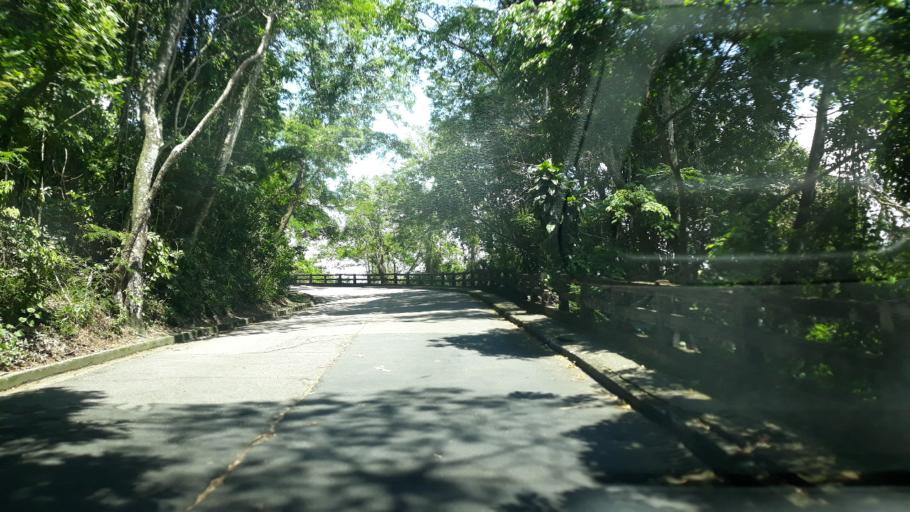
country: BR
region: Rio de Janeiro
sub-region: Rio De Janeiro
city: Rio de Janeiro
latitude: -22.9486
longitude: -43.2060
